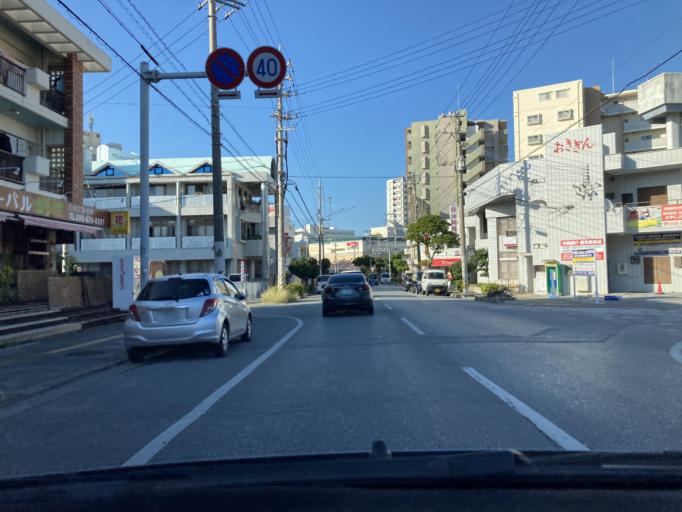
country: JP
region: Okinawa
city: Ginowan
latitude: 26.2565
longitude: 127.7134
